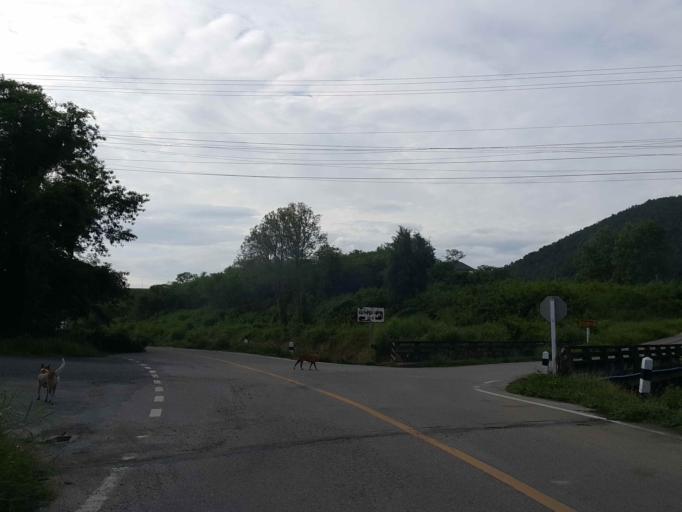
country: TH
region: Chiang Mai
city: San Sai
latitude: 18.9335
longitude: 99.1421
